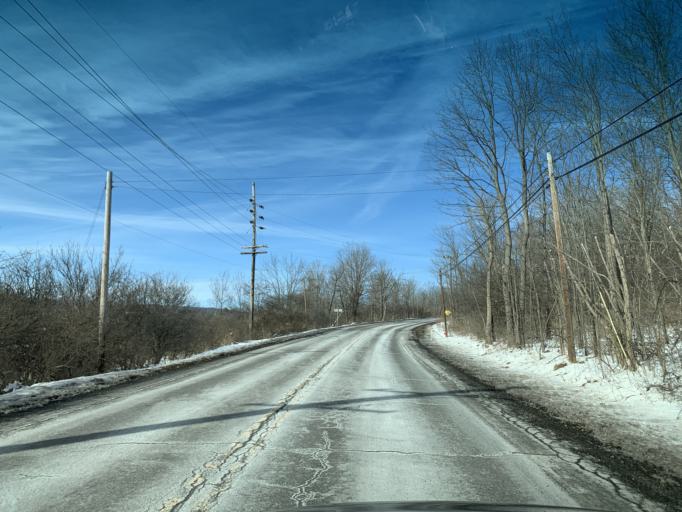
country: US
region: Maryland
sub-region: Allegany County
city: Frostburg
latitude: 39.6202
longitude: -78.9381
